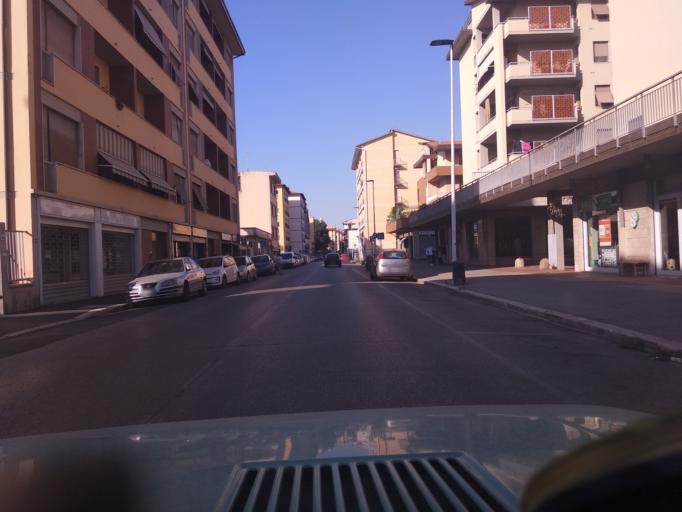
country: IT
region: Tuscany
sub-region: Province of Florence
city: Florence
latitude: 43.7749
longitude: 11.2138
